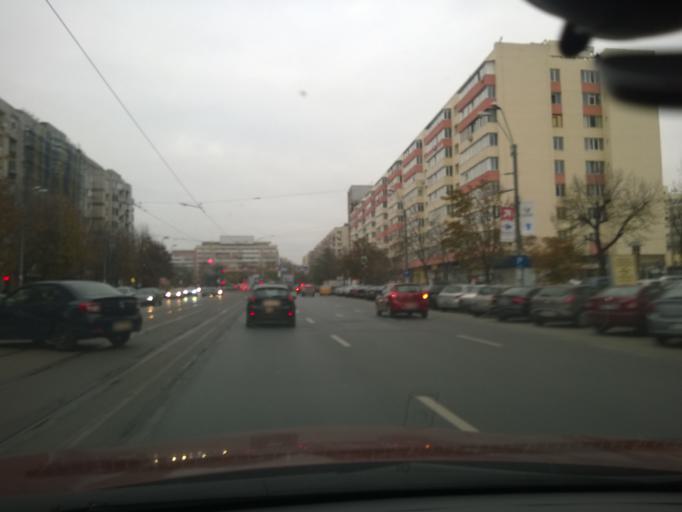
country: RO
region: Bucuresti
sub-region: Municipiul Bucuresti
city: Bucharest
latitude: 44.4393
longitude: 26.1352
